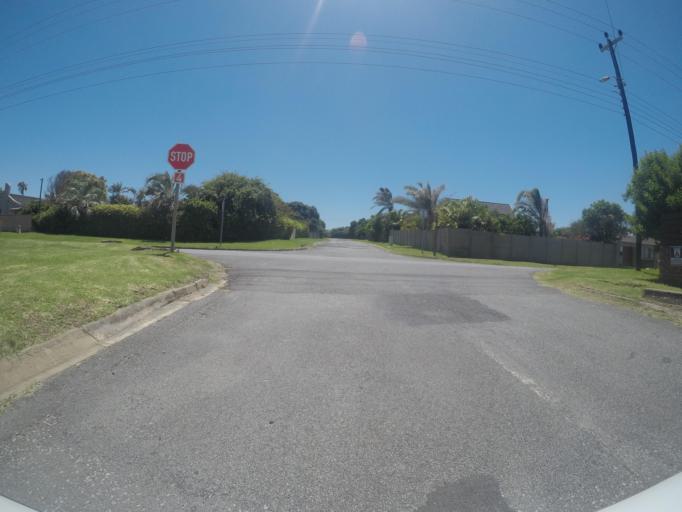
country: ZA
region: Eastern Cape
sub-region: Buffalo City Metropolitan Municipality
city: East London
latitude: -32.9518
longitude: 28.0107
